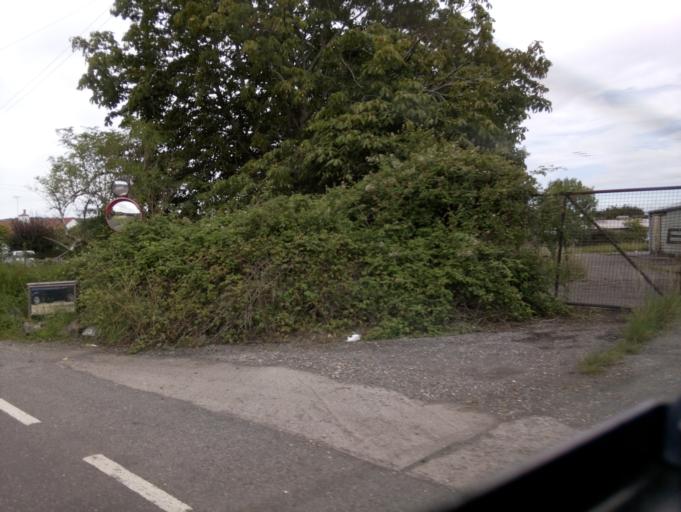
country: GB
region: England
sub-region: North Somerset
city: Churchill
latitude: 51.3515
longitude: -2.7845
